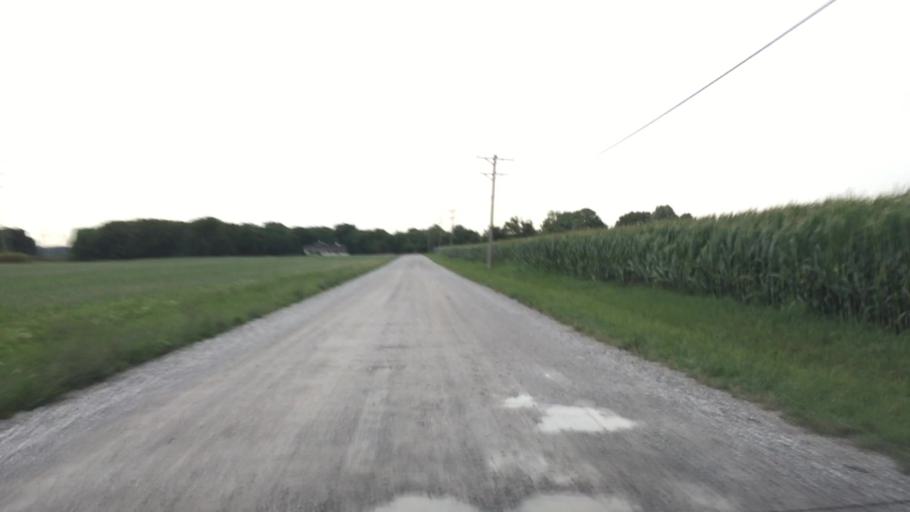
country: US
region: Illinois
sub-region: Hancock County
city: Hamilton
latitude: 40.3721
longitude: -91.3613
